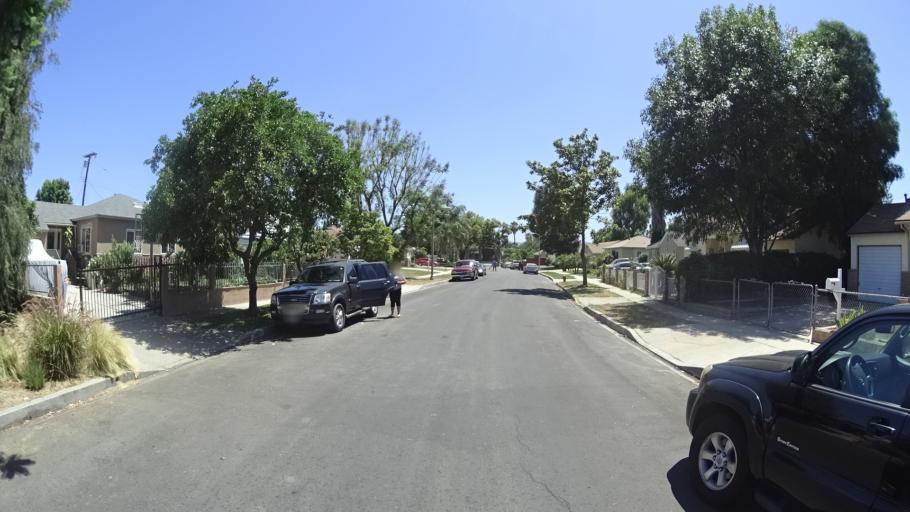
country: US
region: California
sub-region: Los Angeles County
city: Northridge
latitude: 34.1880
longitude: -118.5244
